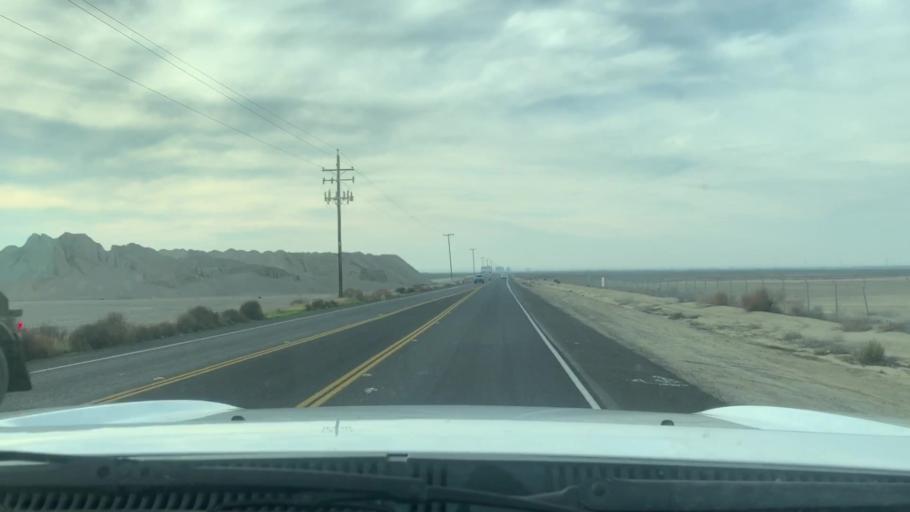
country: US
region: California
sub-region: Kern County
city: Buttonwillow
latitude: 35.4994
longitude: -119.5474
